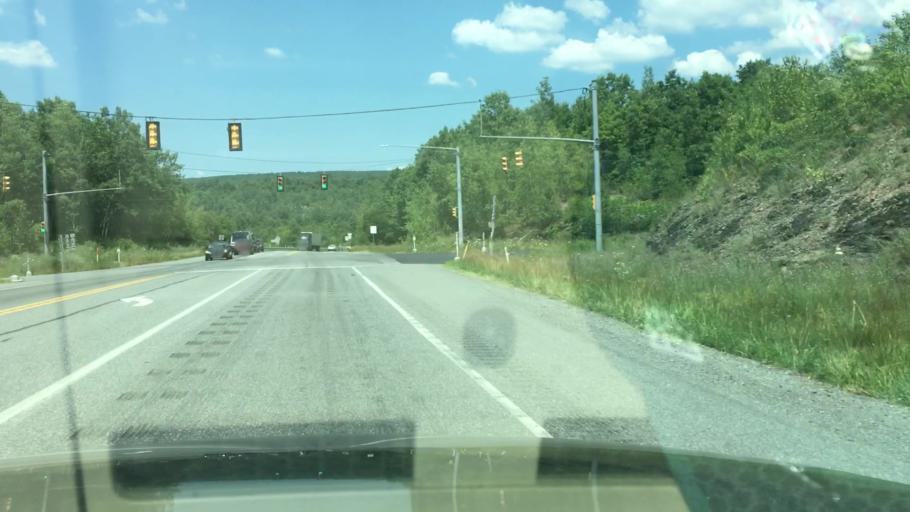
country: US
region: Pennsylvania
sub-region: Northumberland County
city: Kulpmont
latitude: 40.7852
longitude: -76.4475
